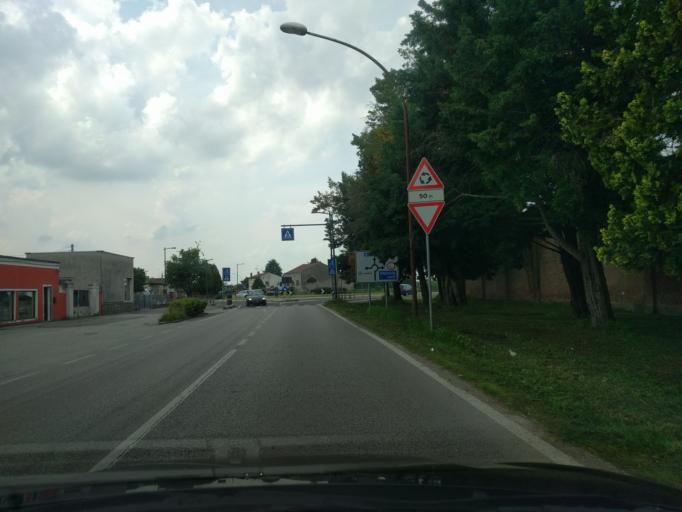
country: IT
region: Veneto
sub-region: Provincia di Rovigo
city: Lendinara
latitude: 45.0881
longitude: 11.6016
